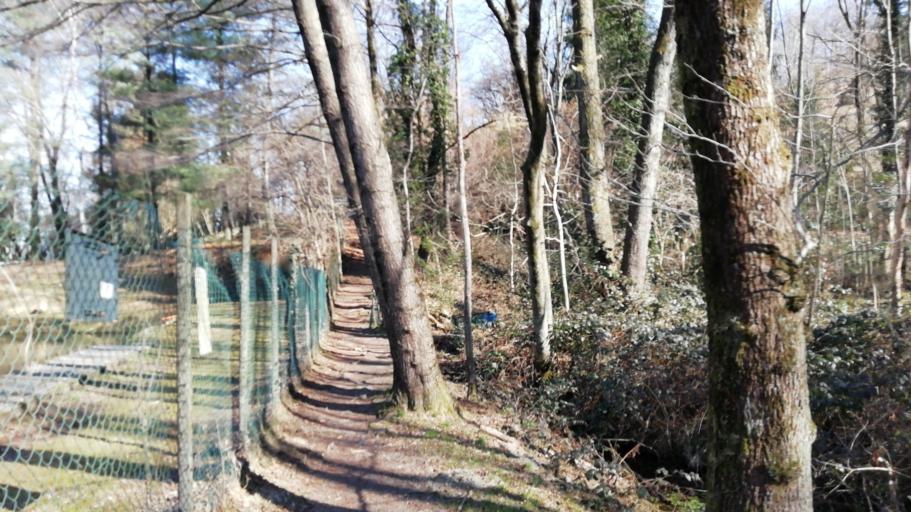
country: IT
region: Piedmont
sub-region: Provincia di Novara
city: San Maurizio D'Opaglio
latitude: 45.7821
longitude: 8.3939
